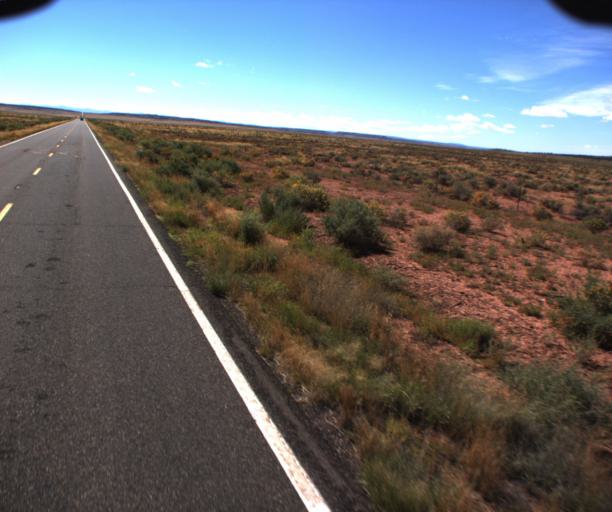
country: US
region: Arizona
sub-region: Apache County
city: Saint Johns
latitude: 34.7154
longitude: -109.2628
